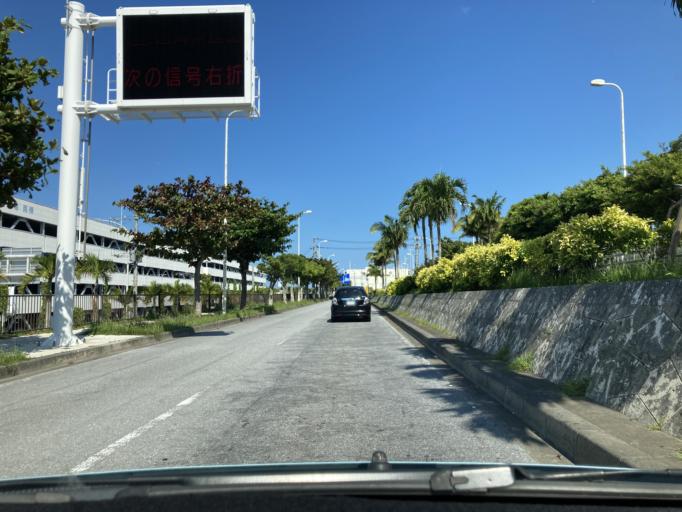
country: JP
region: Okinawa
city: Naha-shi
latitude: 26.2098
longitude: 127.6522
